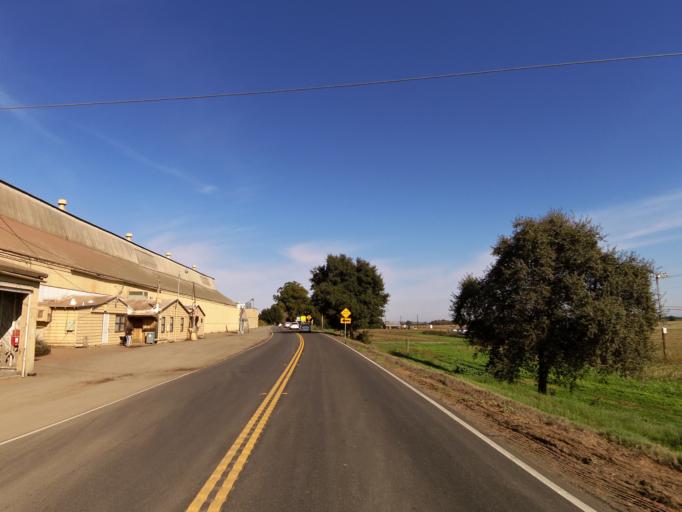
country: US
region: California
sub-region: Solano County
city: Rio Vista
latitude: 38.1687
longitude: -121.5946
